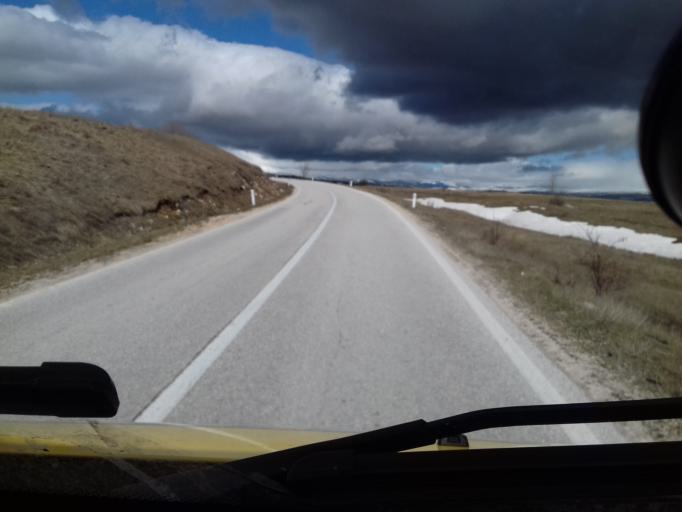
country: BA
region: Federation of Bosnia and Herzegovina
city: Dreznica
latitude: 43.6174
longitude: 17.2643
